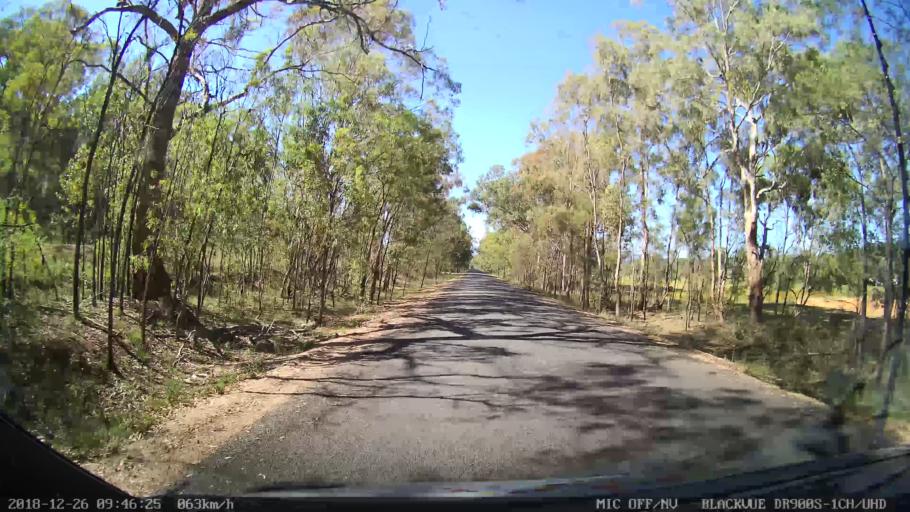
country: AU
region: New South Wales
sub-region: Mid-Western Regional
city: Kandos
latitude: -32.9695
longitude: 150.1053
